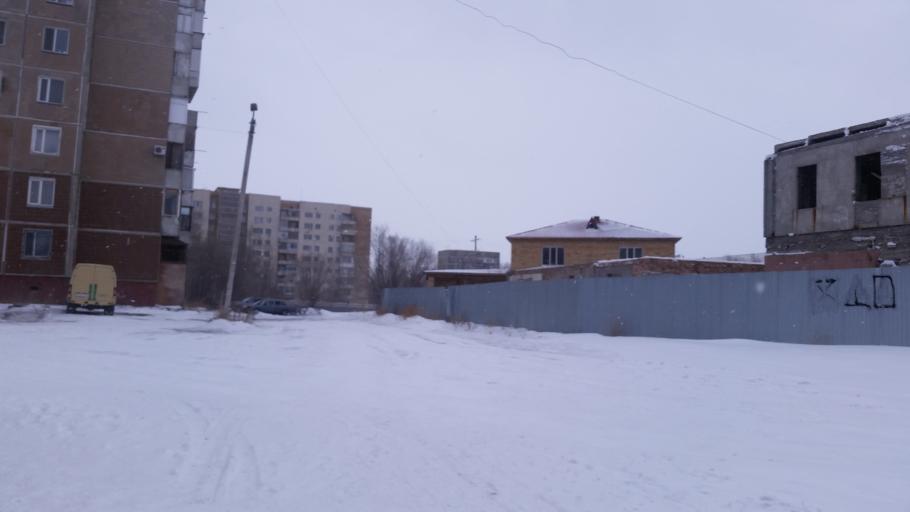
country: KZ
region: Qaraghandy
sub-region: Qaraghandy Qalasy
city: Karagandy
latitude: 49.7742
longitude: 73.1528
